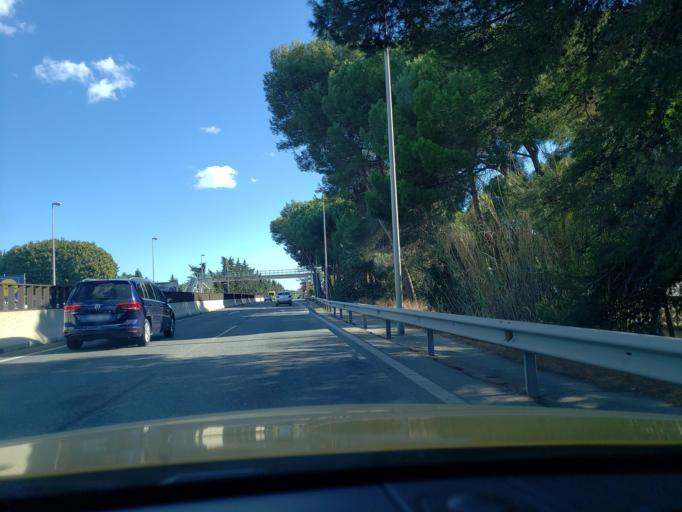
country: ES
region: Andalusia
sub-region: Provincia de Malaga
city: Ojen
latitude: 36.4992
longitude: -4.7936
